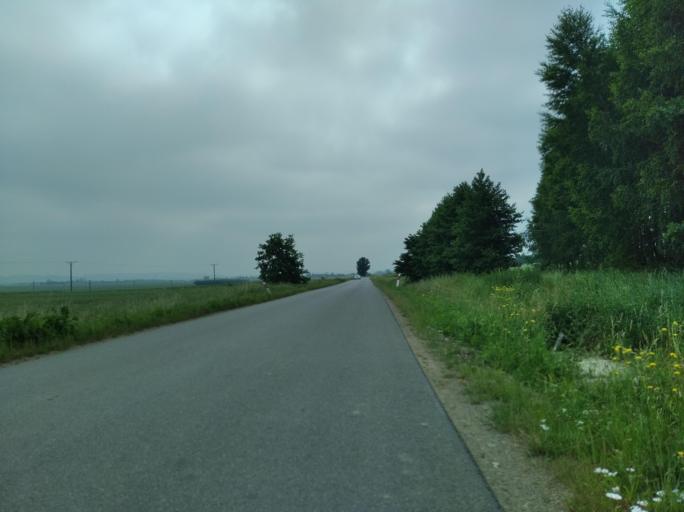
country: PL
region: Subcarpathian Voivodeship
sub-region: Powiat sanocki
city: Besko
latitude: 49.5968
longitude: 21.9242
